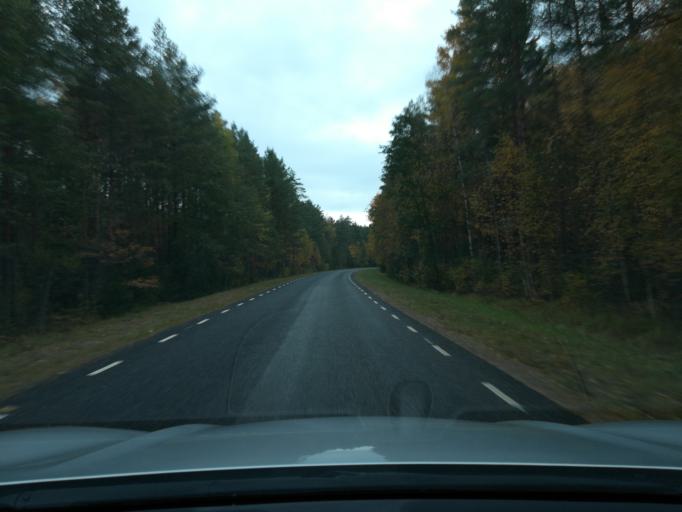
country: EE
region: Ida-Virumaa
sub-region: Johvi vald
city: Johvi
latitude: 59.0306
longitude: 27.3910
